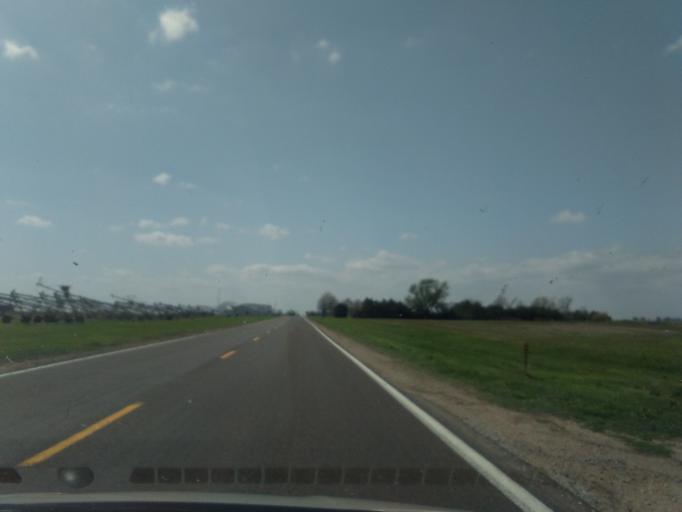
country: US
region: Nebraska
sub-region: Thayer County
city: Hebron
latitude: 40.3213
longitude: -97.4915
